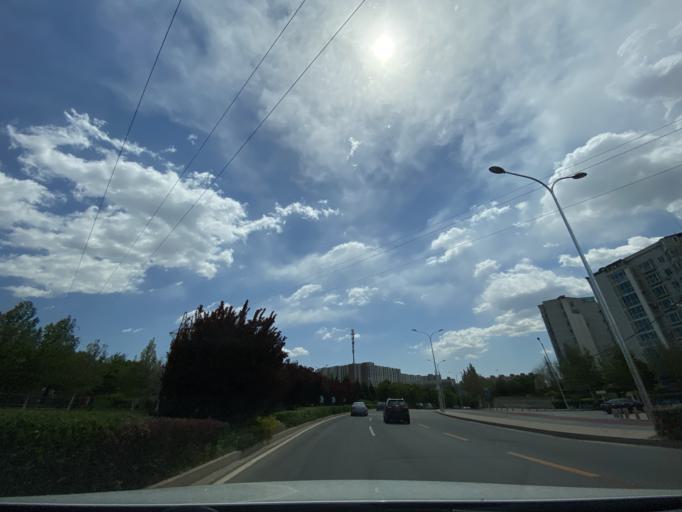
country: CN
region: Beijing
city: Sijiqing
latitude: 39.9335
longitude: 116.2461
